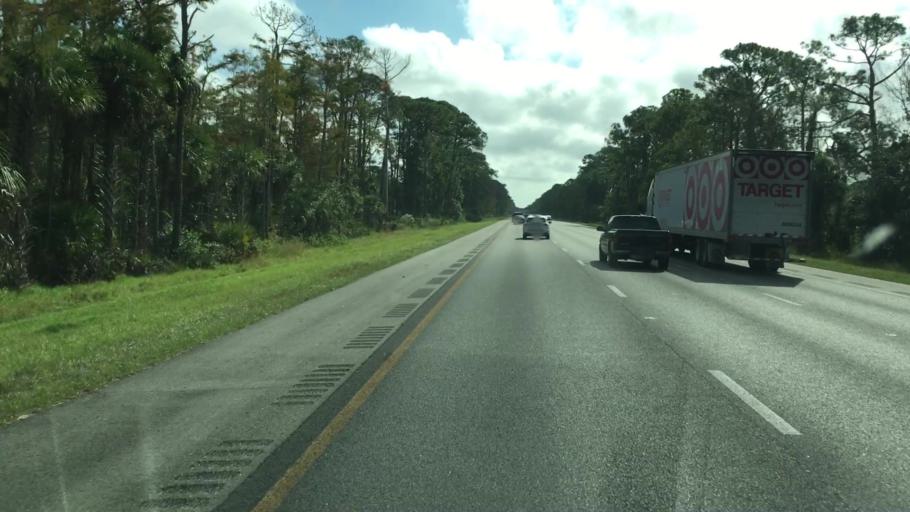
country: US
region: Florida
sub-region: Volusia County
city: Port Orange
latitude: 29.1276
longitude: -81.0569
